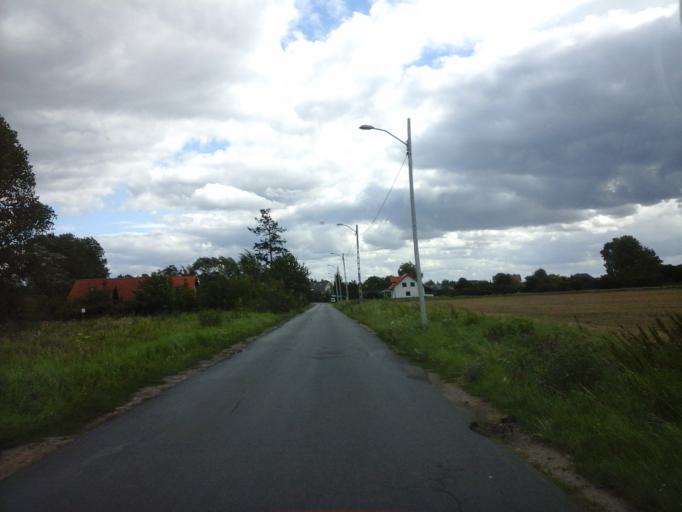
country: PL
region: West Pomeranian Voivodeship
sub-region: Powiat policki
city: Przeclaw
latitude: 53.3879
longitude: 14.4499
